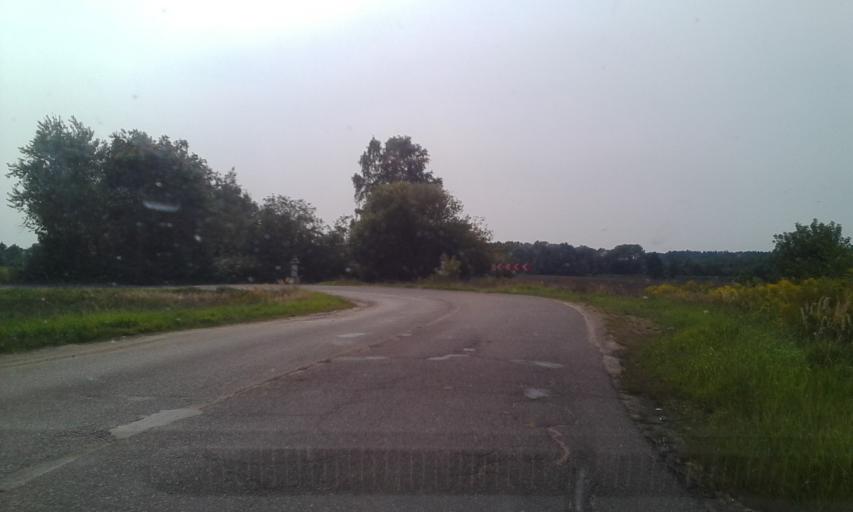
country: BY
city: Michanovichi
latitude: 53.7622
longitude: 27.6724
